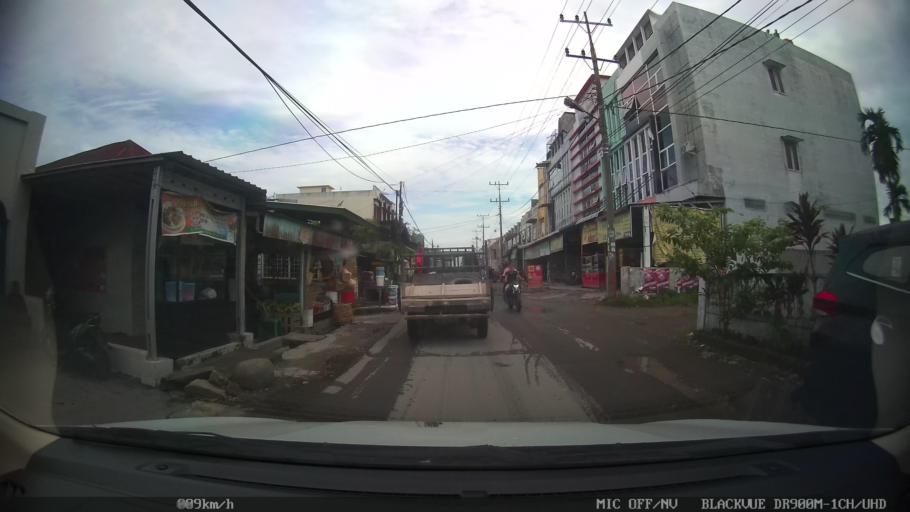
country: ID
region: North Sumatra
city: Sunggal
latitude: 3.6014
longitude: 98.5801
